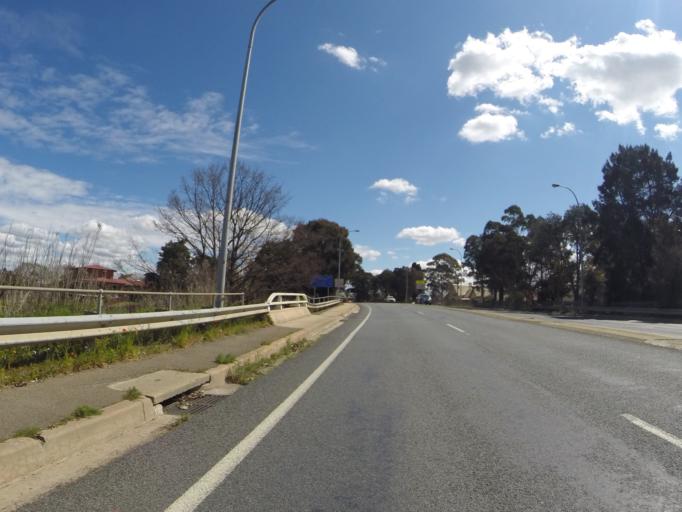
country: AU
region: New South Wales
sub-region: Goulburn Mulwaree
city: Goulburn
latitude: -34.7456
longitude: 149.7361
